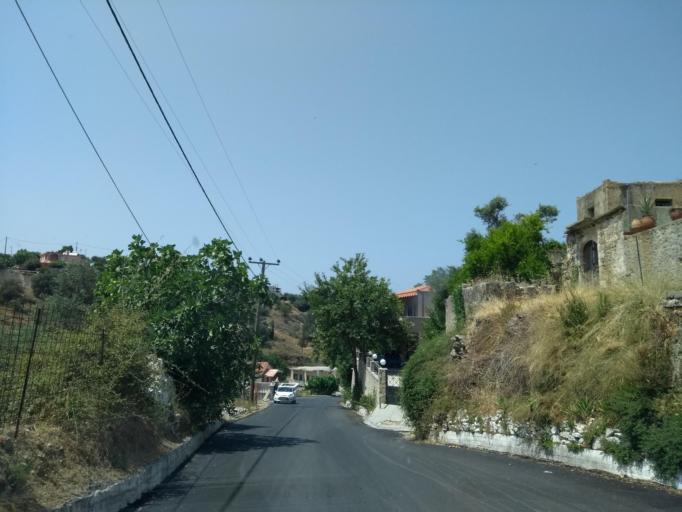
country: GR
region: Crete
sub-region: Nomos Chanias
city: Georgioupolis
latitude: 35.3152
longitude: 24.2991
